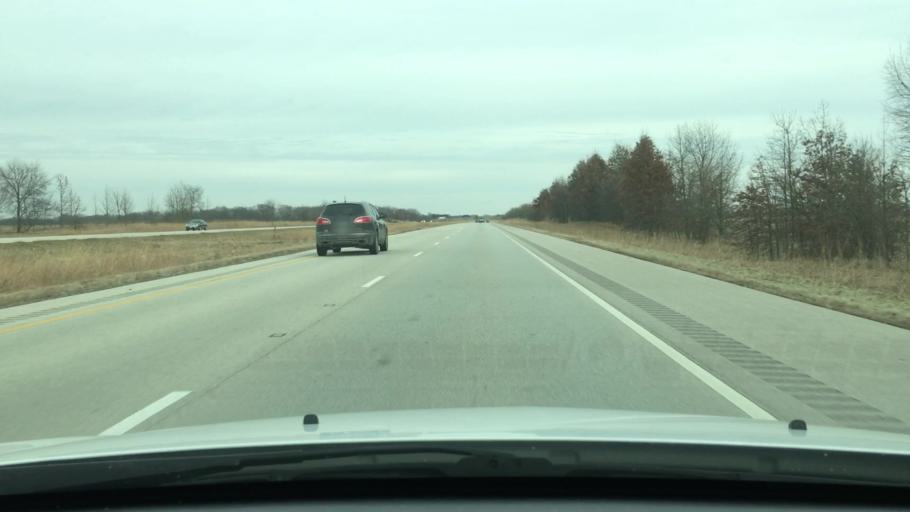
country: US
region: Illinois
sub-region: Sangamon County
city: New Berlin
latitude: 39.7458
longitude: -89.8137
